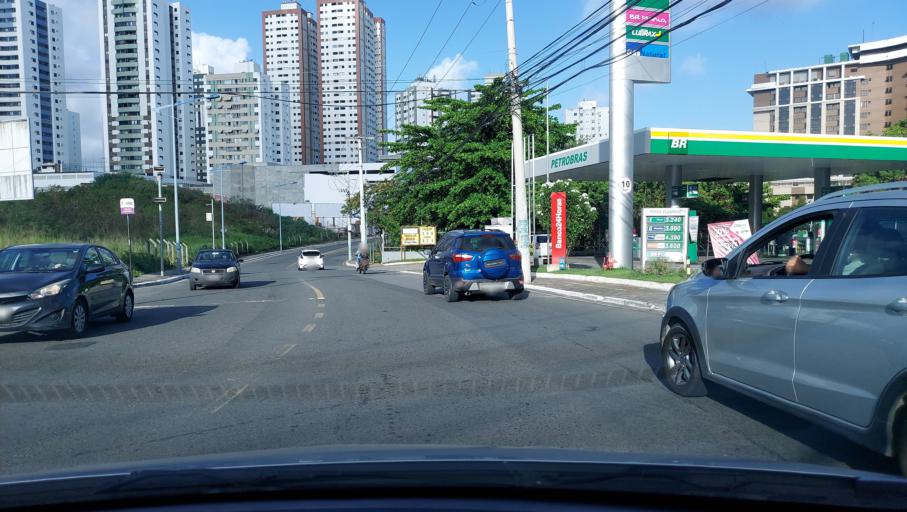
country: BR
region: Bahia
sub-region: Salvador
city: Salvador
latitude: -12.9817
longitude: -38.4433
